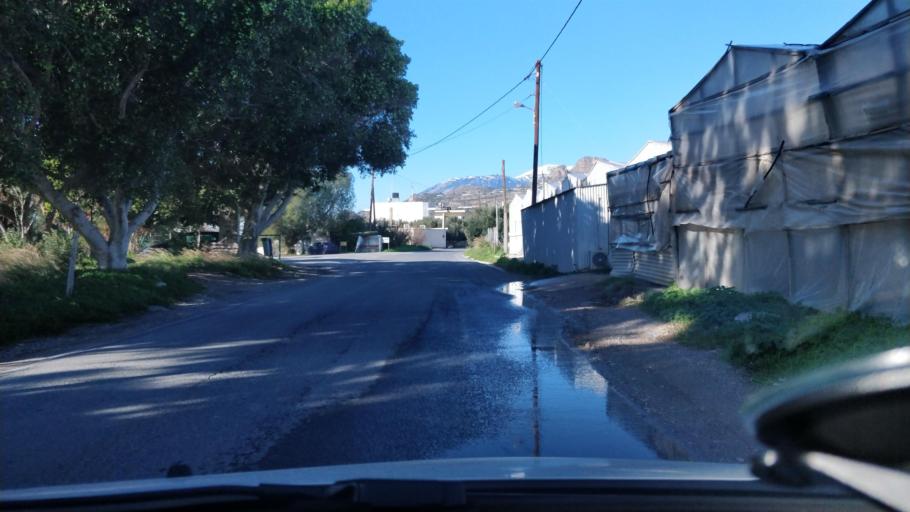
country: GR
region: Crete
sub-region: Nomos Lasithiou
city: Gra Liyia
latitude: 35.0203
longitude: 25.6794
